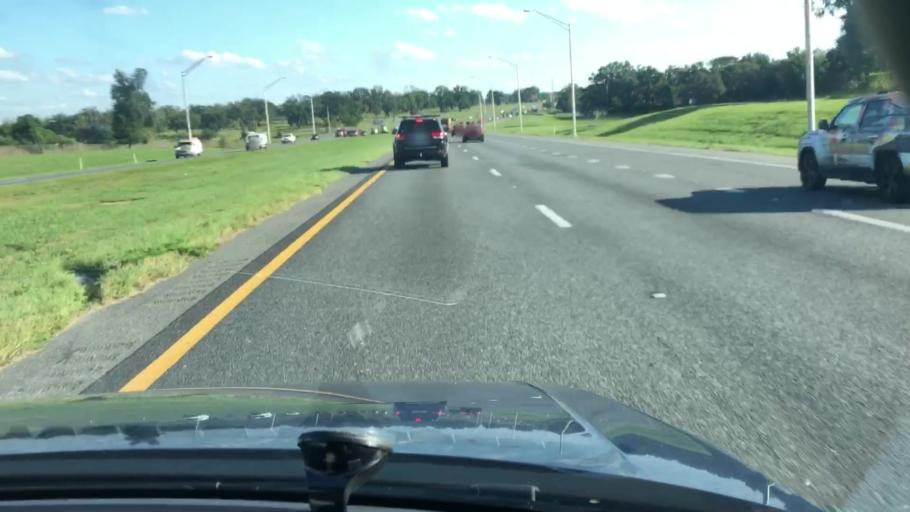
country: US
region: Florida
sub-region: Orange County
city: Paradise Heights
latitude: 28.6299
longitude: -81.5393
